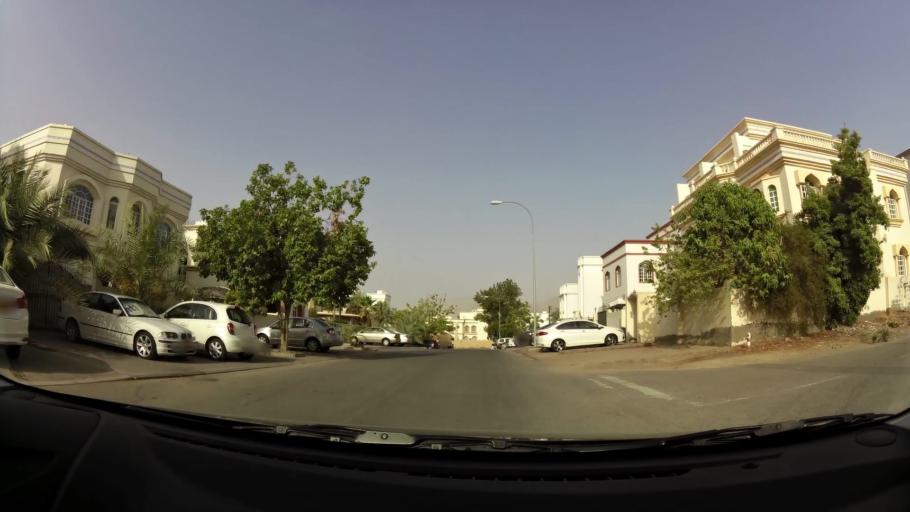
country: OM
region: Muhafazat Masqat
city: Bawshar
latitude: 23.5449
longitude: 58.3630
